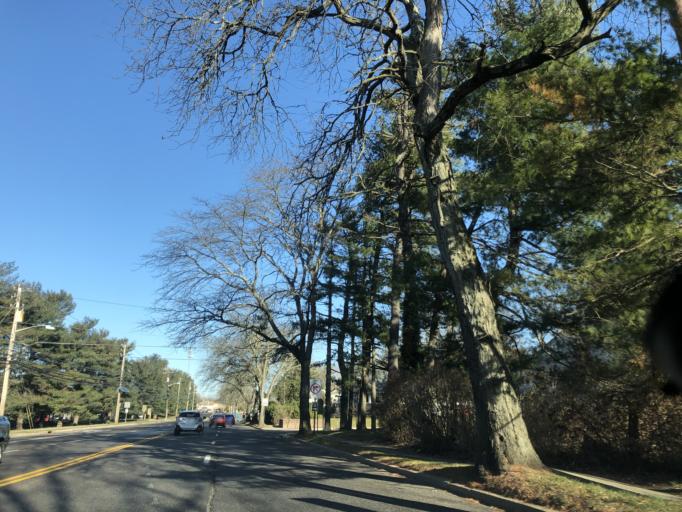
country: US
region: New Jersey
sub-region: Camden County
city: Ashland
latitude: 39.8735
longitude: -75.0067
